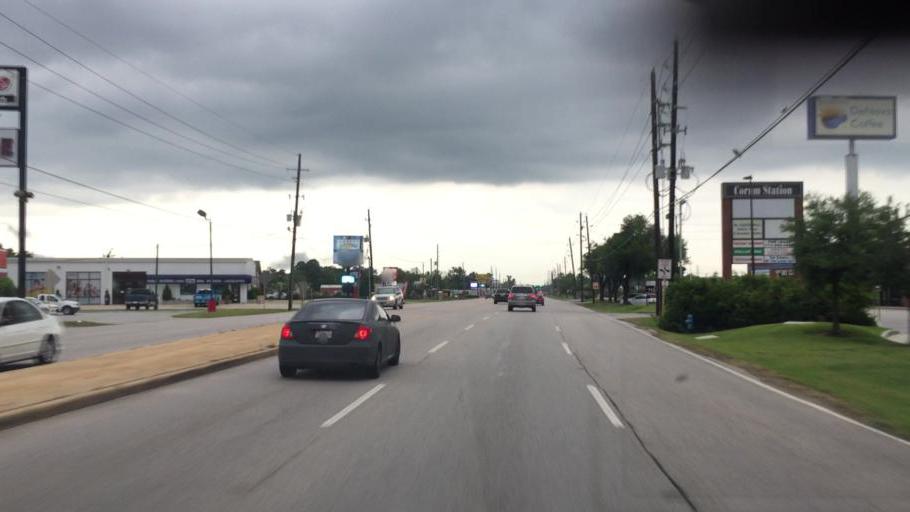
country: US
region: Texas
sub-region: Harris County
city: Spring
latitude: 30.0412
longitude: -95.4889
